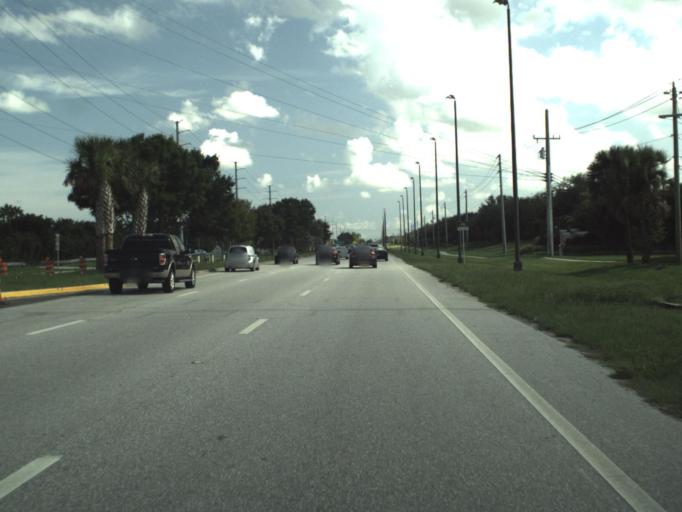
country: US
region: Florida
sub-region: Palm Beach County
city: Boca Pointe
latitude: 26.3652
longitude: -80.2036
